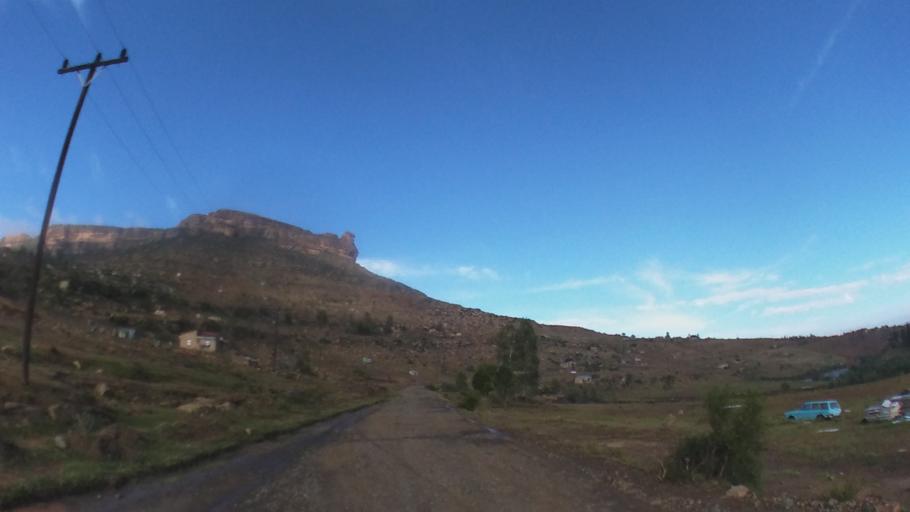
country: LS
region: Maseru
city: Maseru
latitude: -29.4029
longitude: 27.4712
